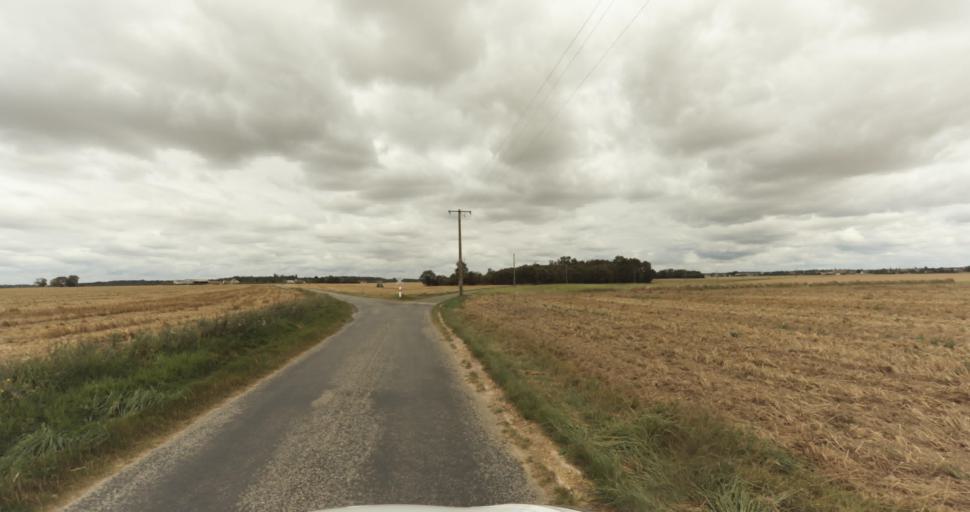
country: FR
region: Haute-Normandie
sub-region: Departement de l'Eure
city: Nonancourt
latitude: 48.7928
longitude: 1.1417
